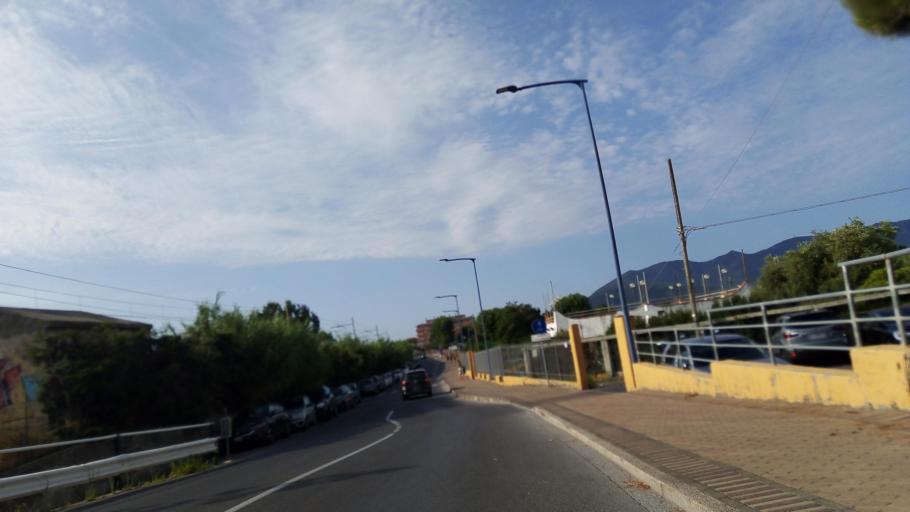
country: IT
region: Liguria
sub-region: Provincia di Savona
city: Ceriale
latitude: 44.0842
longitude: 8.2273
